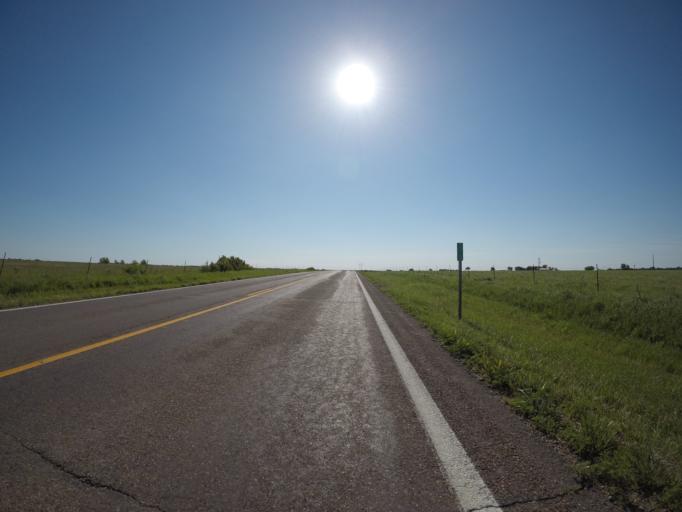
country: US
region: Kansas
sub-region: Lyon County
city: Emporia
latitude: 38.6516
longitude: -96.1138
